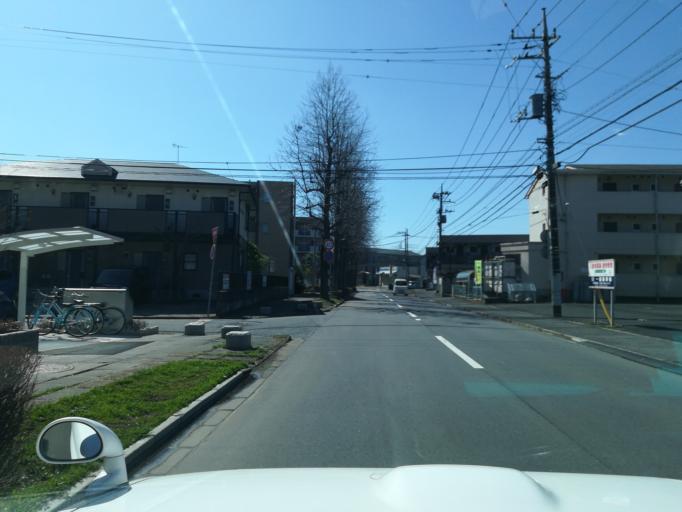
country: JP
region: Ibaraki
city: Naka
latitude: 36.0981
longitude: 140.0985
